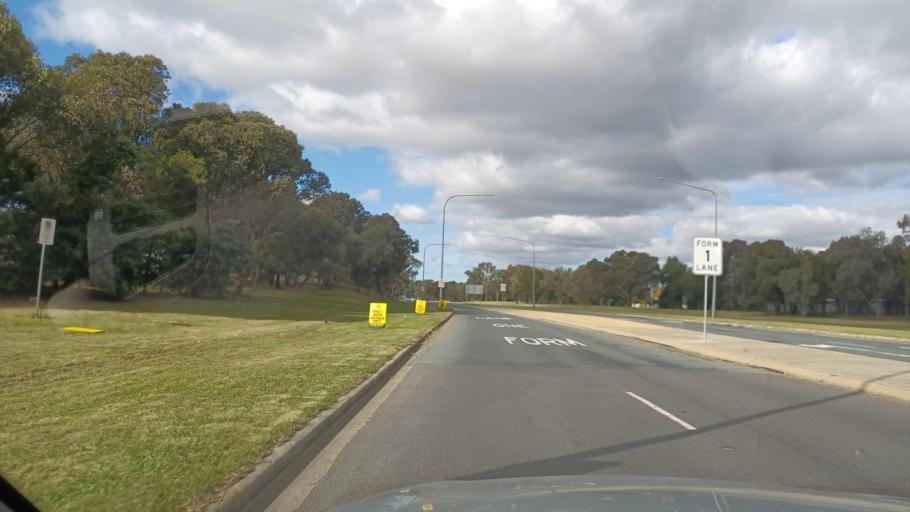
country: AU
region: Australian Capital Territory
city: Belconnen
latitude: -35.2054
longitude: 149.0276
